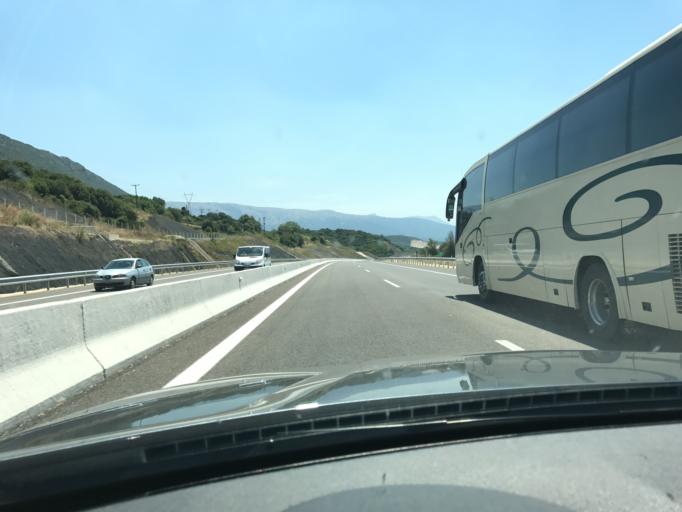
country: GR
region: Epirus
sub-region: Nomos Ioanninon
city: Agia Kyriaki
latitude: 39.4886
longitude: 20.8911
